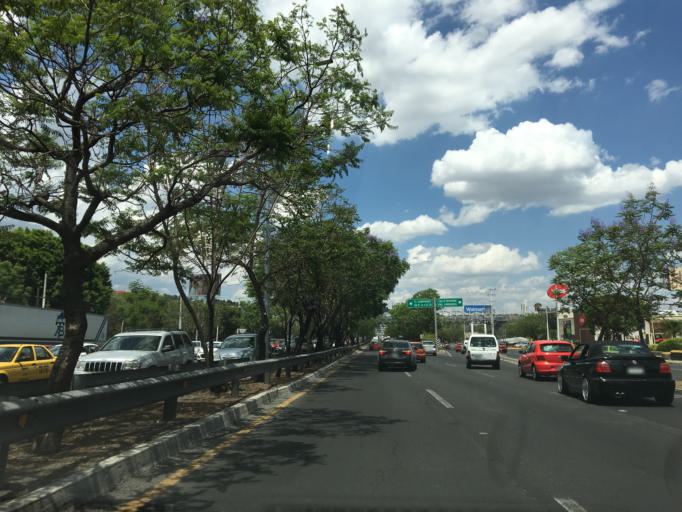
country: MX
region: Queretaro
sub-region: Queretaro
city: Santiago de Queretaro
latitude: 20.6168
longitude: -100.4007
